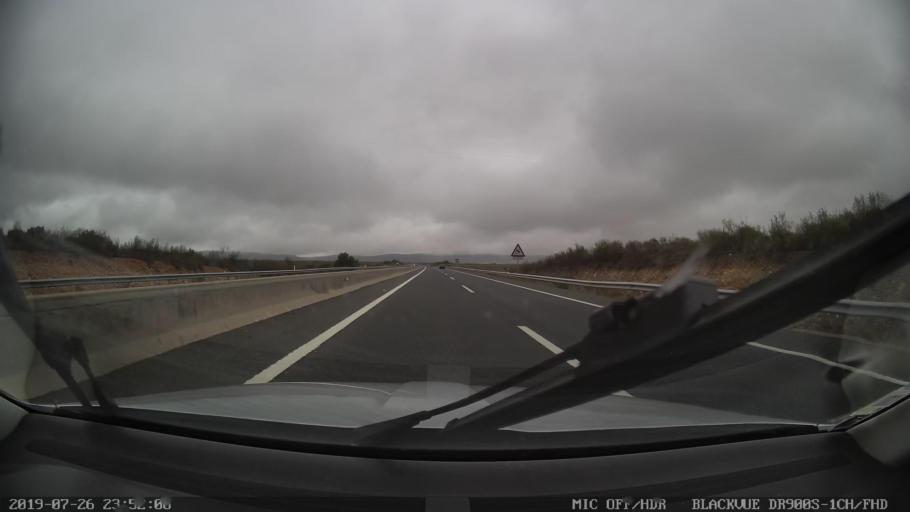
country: ES
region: Extremadura
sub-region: Provincia de Caceres
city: Jaraicejo
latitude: 39.6681
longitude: -5.7537
